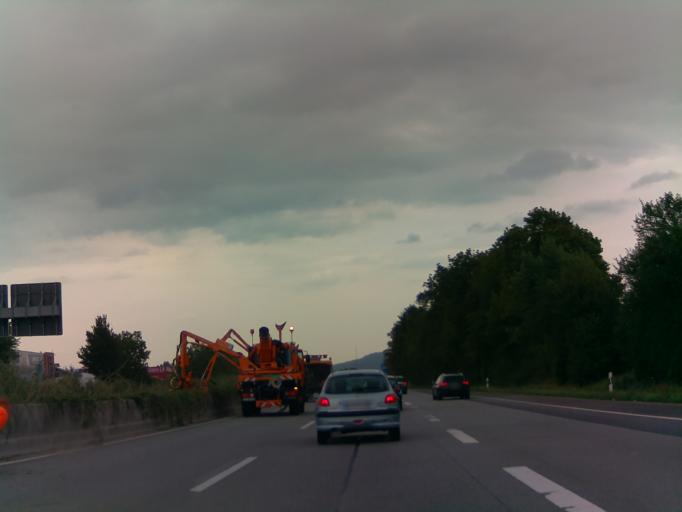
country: DE
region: Hesse
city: Viernheim
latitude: 49.5318
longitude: 8.5837
